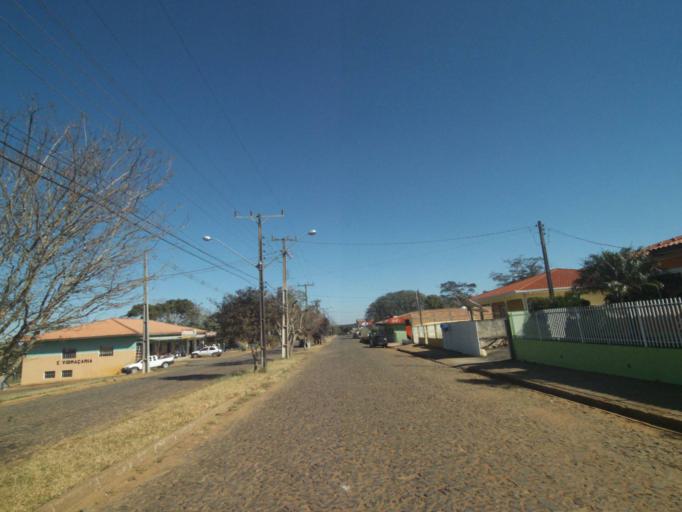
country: BR
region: Parana
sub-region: Reserva
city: Reserva
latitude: -24.6238
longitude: -50.6408
